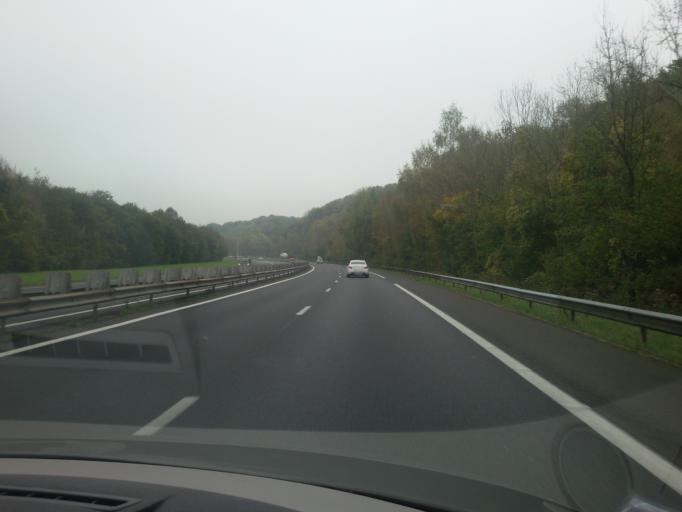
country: FR
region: Lower Normandy
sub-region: Departement du Calvados
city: Villers-sur-Mer
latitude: 49.2455
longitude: 0.0468
